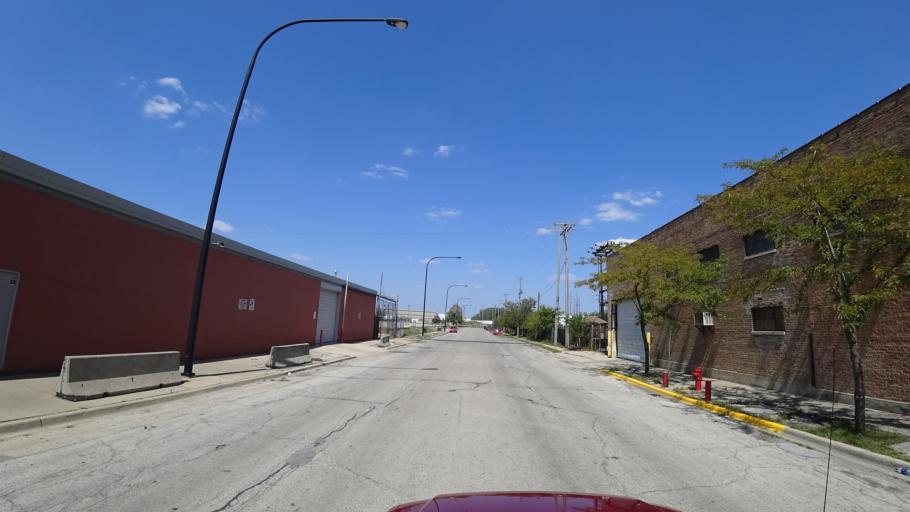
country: US
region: Illinois
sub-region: Cook County
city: Cicero
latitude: 41.8565
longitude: -87.7408
